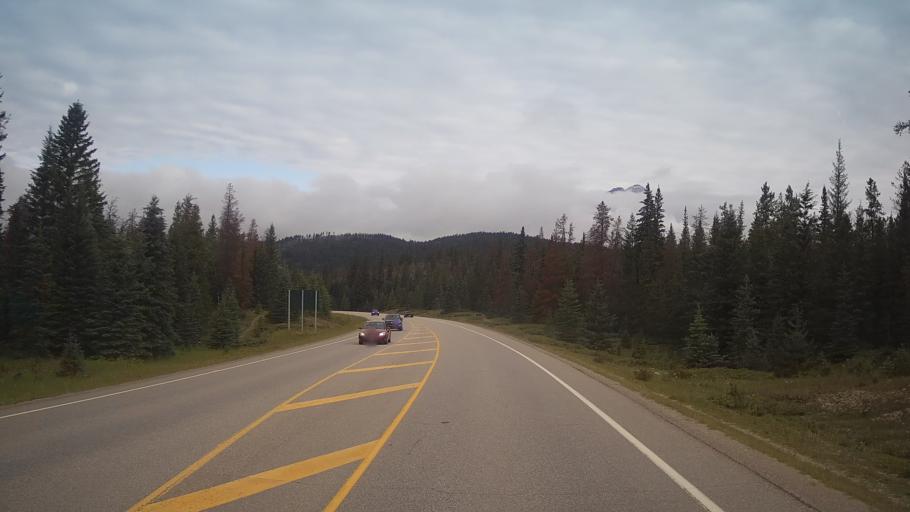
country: CA
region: Alberta
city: Jasper Park Lodge
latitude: 52.8596
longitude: -118.0806
